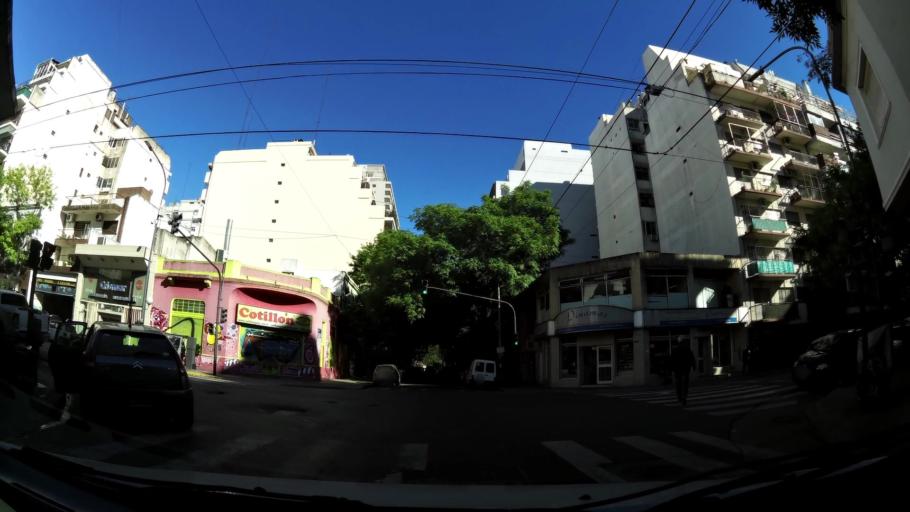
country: AR
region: Buenos Aires F.D.
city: Colegiales
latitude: -34.5567
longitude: -58.4571
